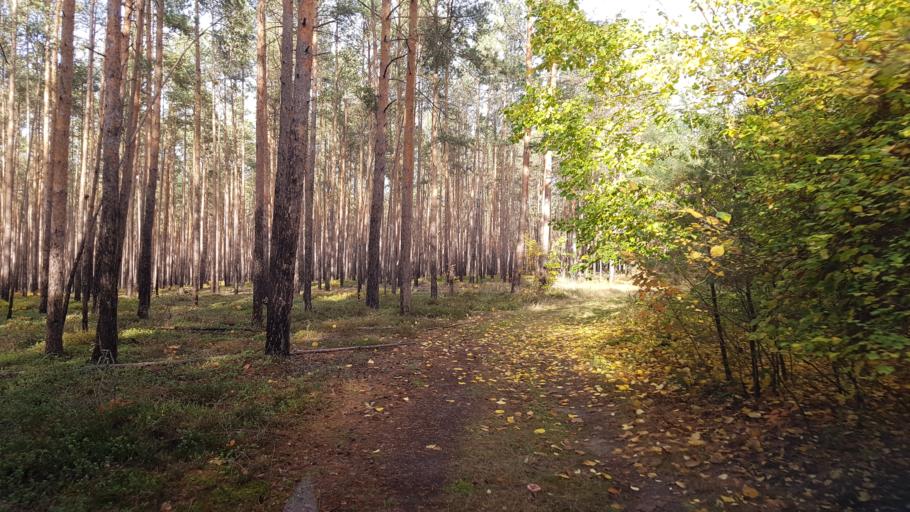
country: DE
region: Brandenburg
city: Finsterwalde
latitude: 51.5817
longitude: 13.7072
